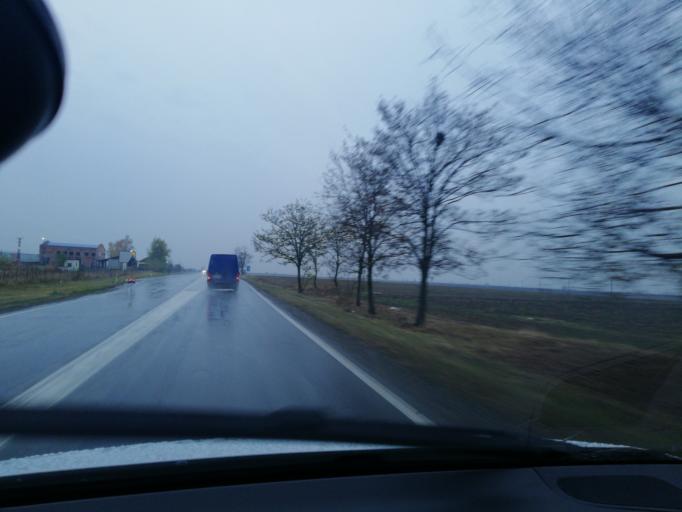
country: RS
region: Autonomna Pokrajina Vojvodina
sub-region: Sremski Okrug
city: Irig
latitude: 45.0792
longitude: 19.8542
